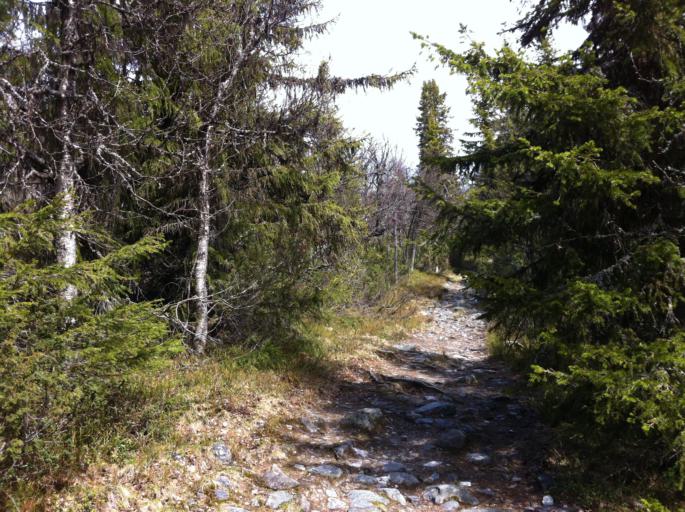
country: SE
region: Jaemtland
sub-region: Are Kommun
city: Are
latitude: 62.6842
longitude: 12.9656
